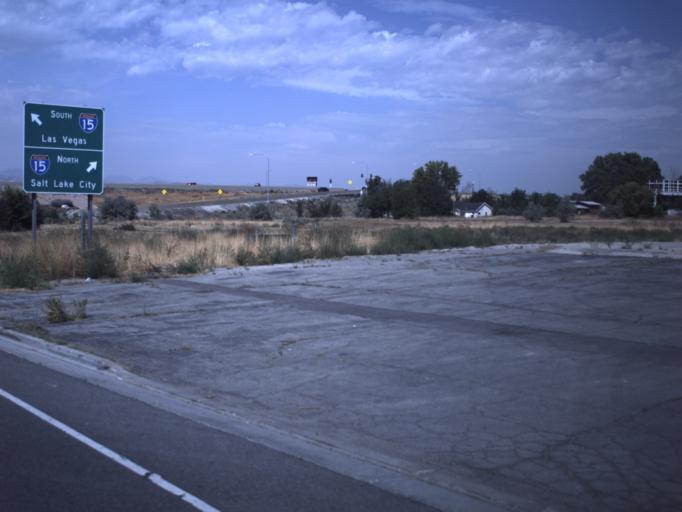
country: US
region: Utah
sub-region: Utah County
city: Lehi
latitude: 40.3884
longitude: -111.8309
